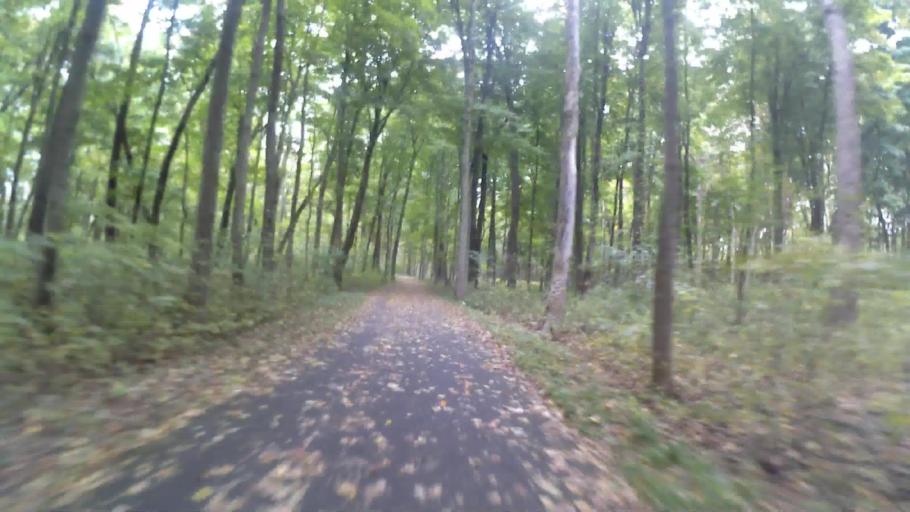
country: US
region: Illinois
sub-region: Kane County
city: Sugar Grove
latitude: 41.7829
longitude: -88.4338
